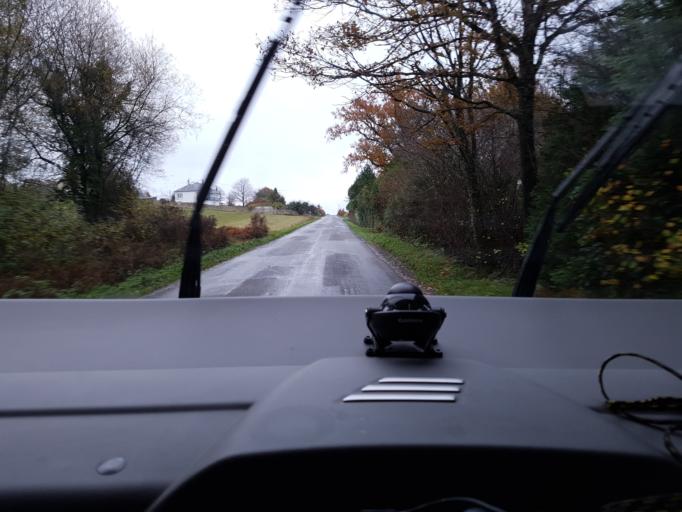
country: FR
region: Brittany
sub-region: Departement d'Ille-et-Vilaine
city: Vitre
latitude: 48.1297
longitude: -1.1716
